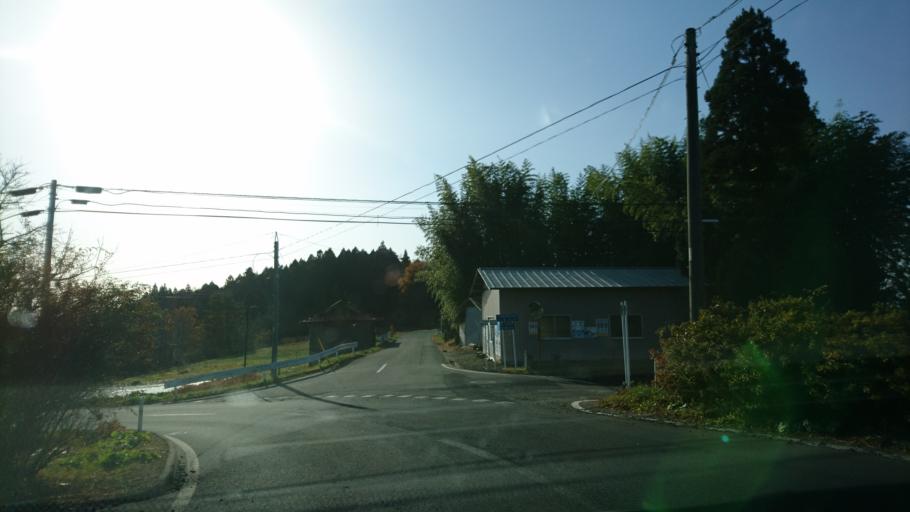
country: JP
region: Iwate
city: Ichinoseki
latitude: 38.8720
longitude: 141.3008
